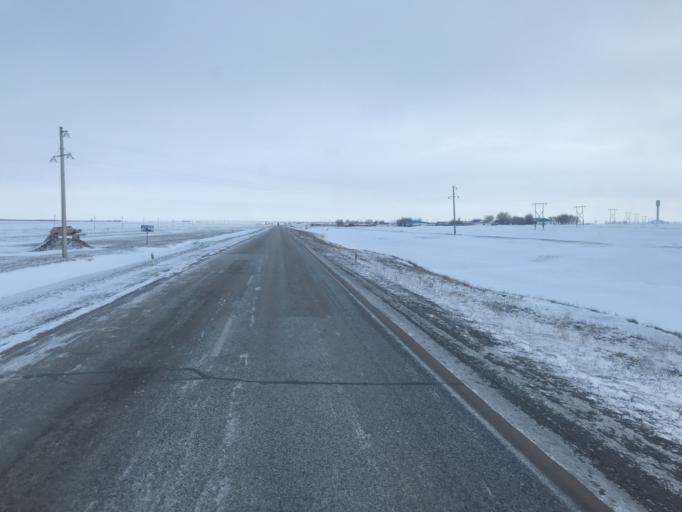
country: RU
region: Orenburg
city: Dombarovskiy
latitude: 49.9742
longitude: 60.0366
